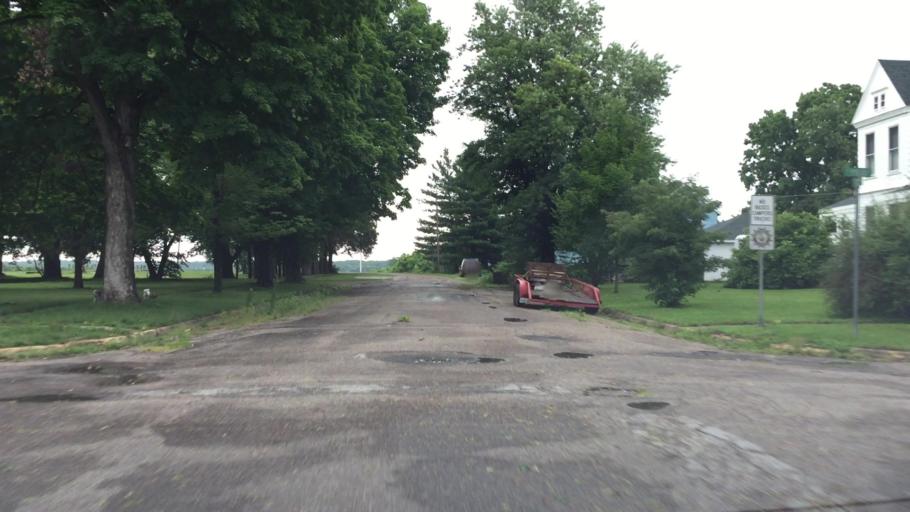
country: US
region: Illinois
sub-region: Hancock County
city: Warsaw
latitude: 40.3637
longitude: -91.4363
